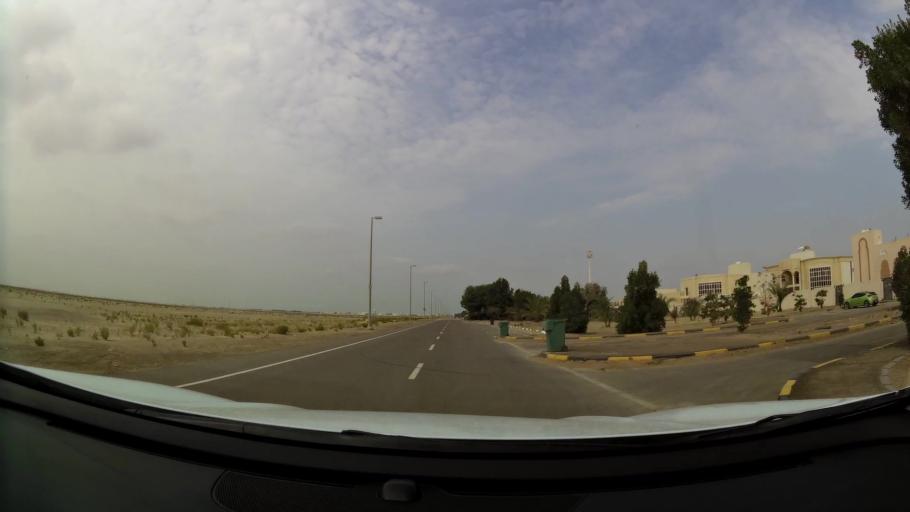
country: AE
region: Abu Dhabi
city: Abu Dhabi
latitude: 24.6321
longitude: 54.6811
